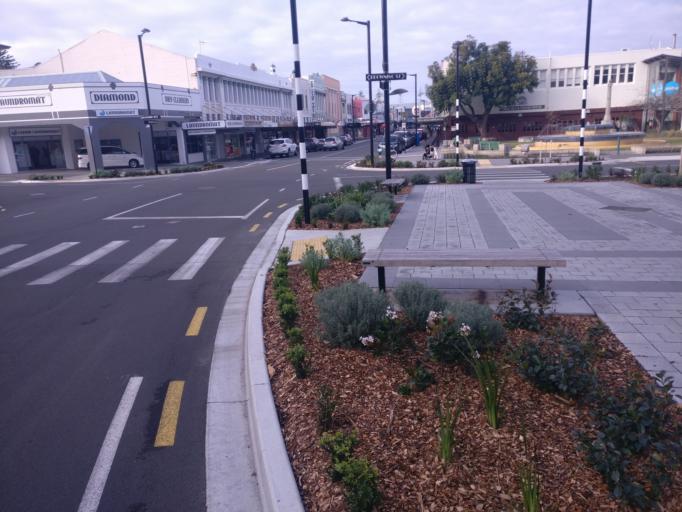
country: NZ
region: Hawke's Bay
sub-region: Napier City
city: Napier
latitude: -39.4882
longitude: 176.9175
